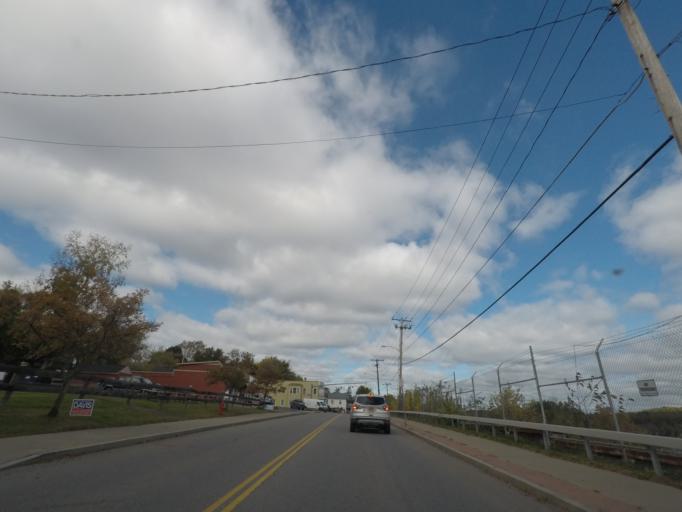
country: US
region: New York
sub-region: Albany County
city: Cohoes
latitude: 42.7864
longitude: -73.7113
